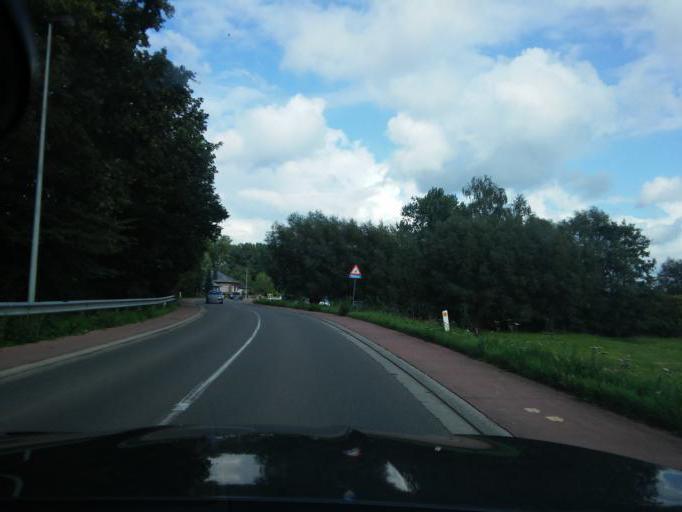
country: BE
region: Flanders
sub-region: Provincie Oost-Vlaanderen
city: Geraardsbergen
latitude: 50.7907
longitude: 3.9253
